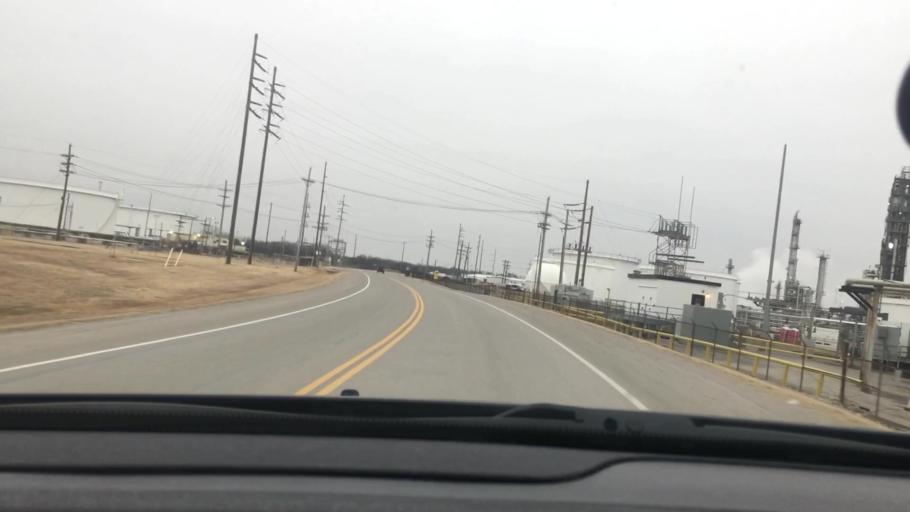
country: US
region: Oklahoma
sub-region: Garvin County
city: Wynnewood
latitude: 34.6348
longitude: -97.1687
